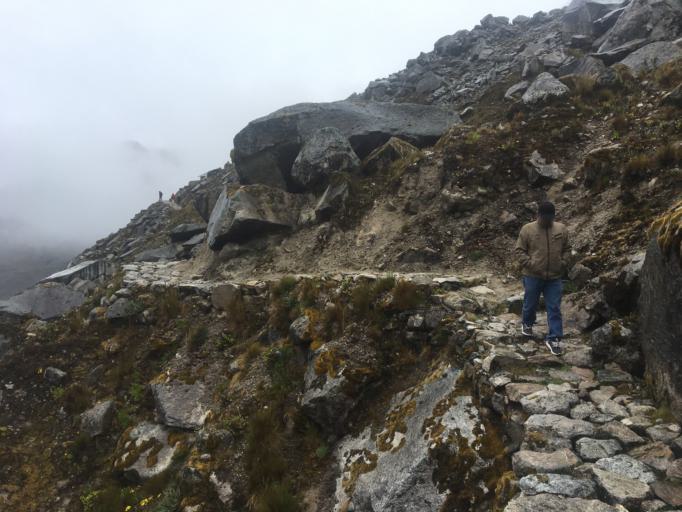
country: PE
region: Ancash
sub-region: Provincia de Yungay
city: Yanama
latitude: -9.1409
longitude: -77.5034
